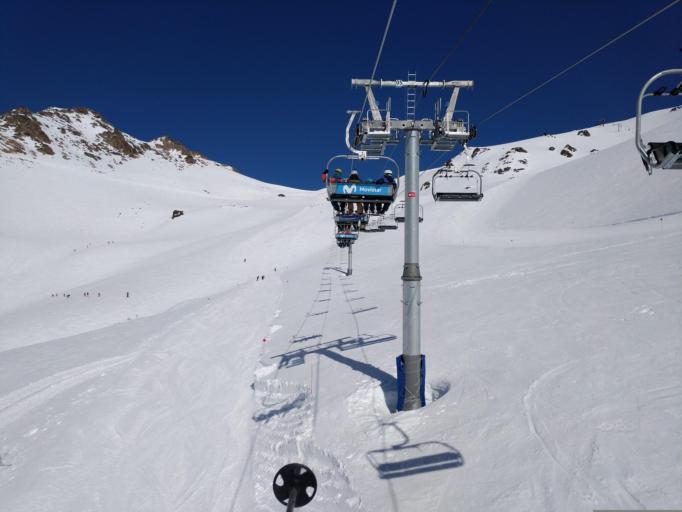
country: AR
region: Rio Negro
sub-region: Departamento de Bariloche
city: San Carlos de Bariloche
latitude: -41.1689
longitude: -71.4750
